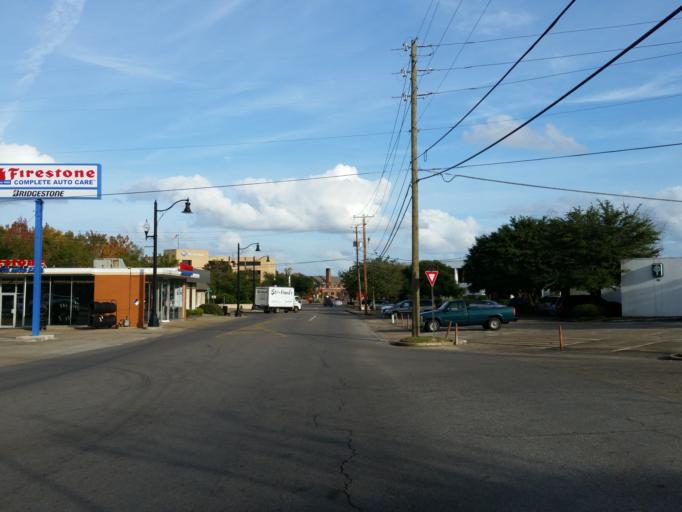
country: US
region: Mississippi
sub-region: Forrest County
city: Hattiesburg
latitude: 31.3247
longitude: -89.2953
